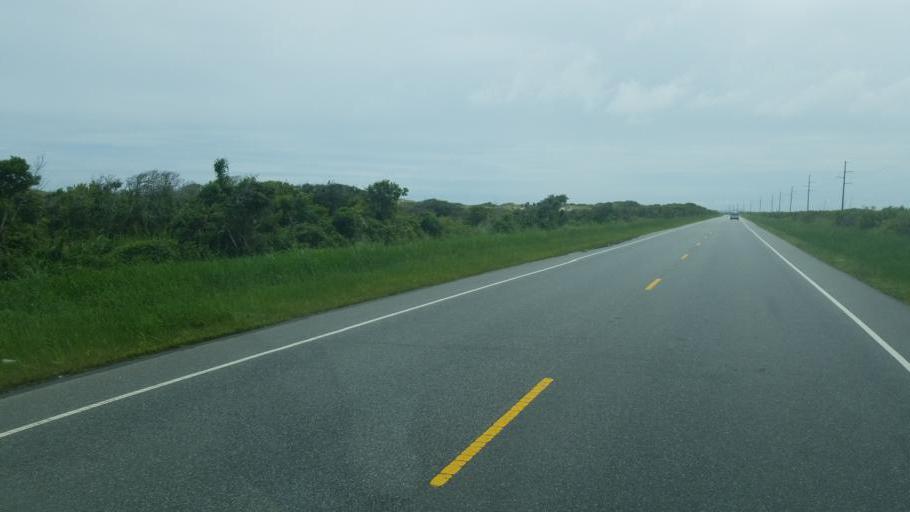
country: US
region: North Carolina
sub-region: Dare County
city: Wanchese
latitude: 35.8156
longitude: -75.5521
